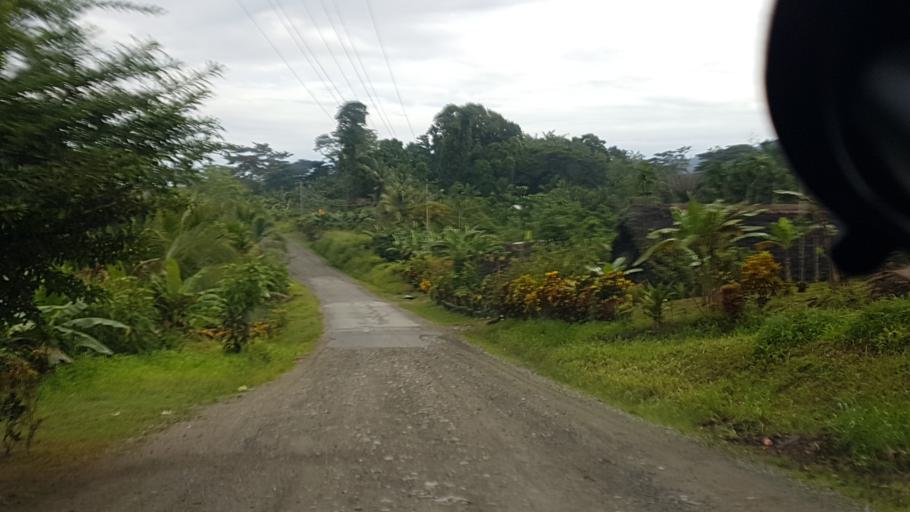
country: PG
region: East Sepik
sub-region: Wewak
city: Wewak
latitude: -3.6986
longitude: 143.3064
